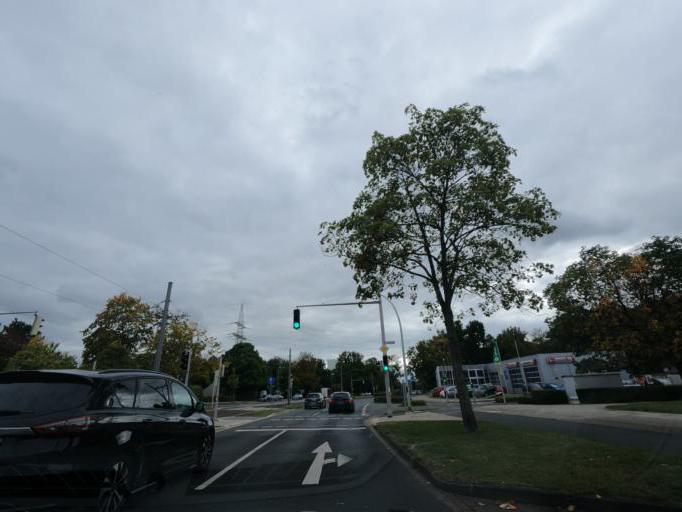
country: DE
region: Lower Saxony
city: Braunschweig
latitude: 52.2449
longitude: 10.4894
